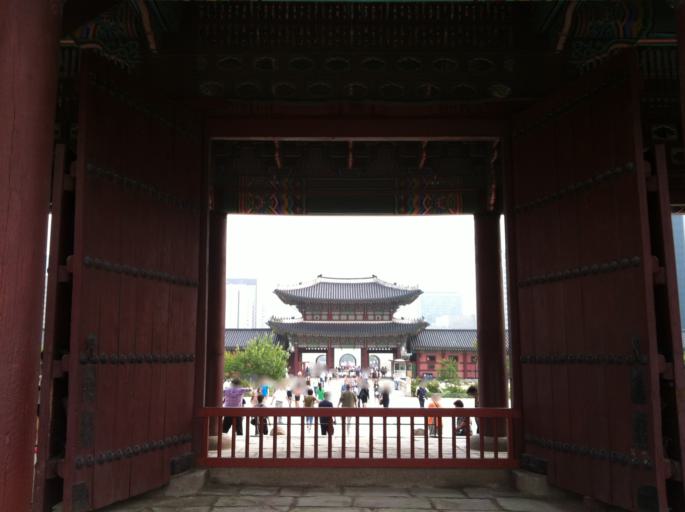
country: KR
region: Seoul
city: Seoul
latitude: 37.5778
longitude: 126.9769
